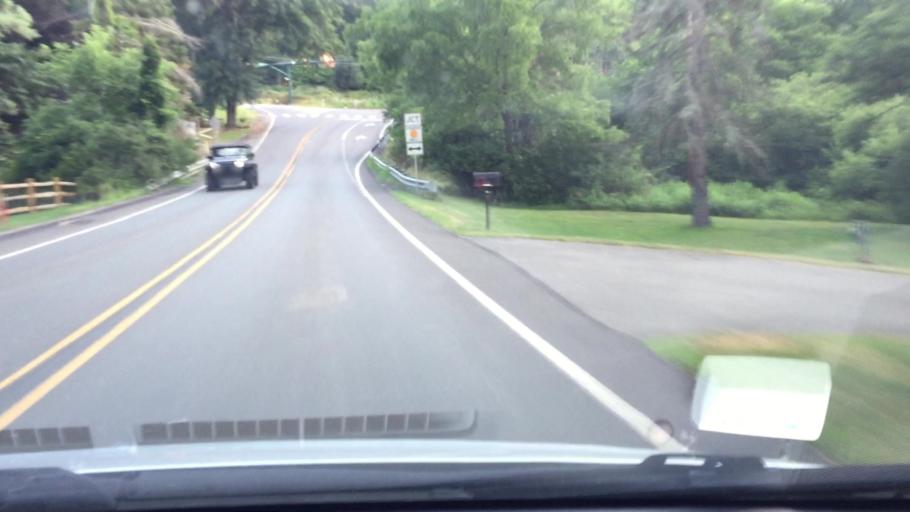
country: US
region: Pennsylvania
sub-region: Allegheny County
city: Gibsonia
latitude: 40.6292
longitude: -80.0242
